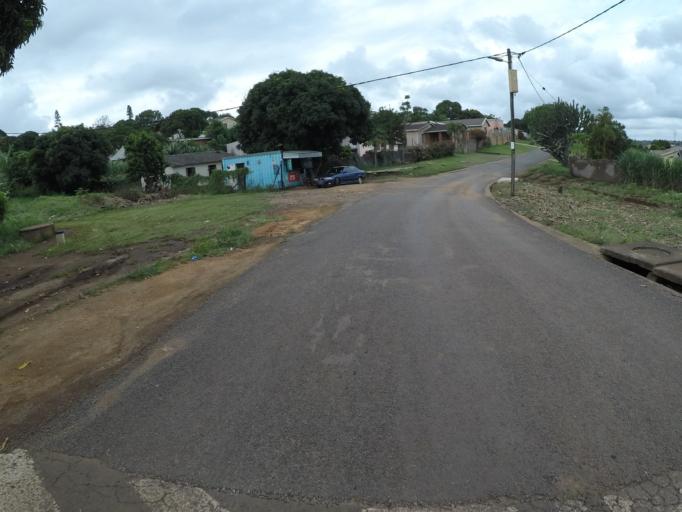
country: ZA
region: KwaZulu-Natal
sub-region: uThungulu District Municipality
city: Empangeni
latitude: -28.7729
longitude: 31.8652
